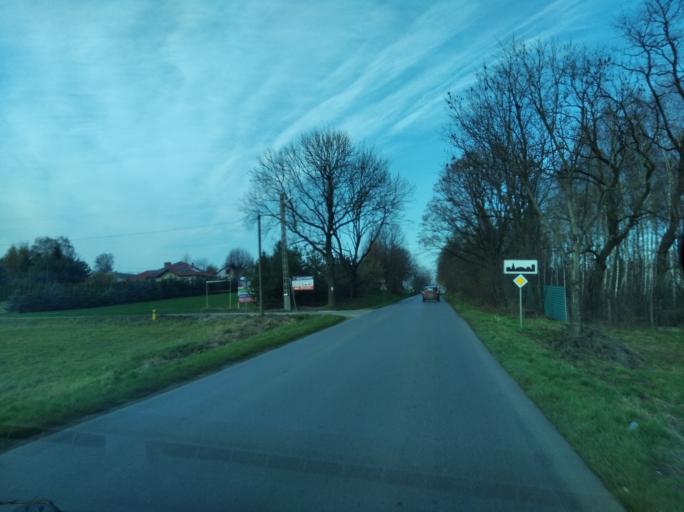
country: PL
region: Subcarpathian Voivodeship
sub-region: Powiat ropczycko-sedziszowski
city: Iwierzyce
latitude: 50.0460
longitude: 21.7451
